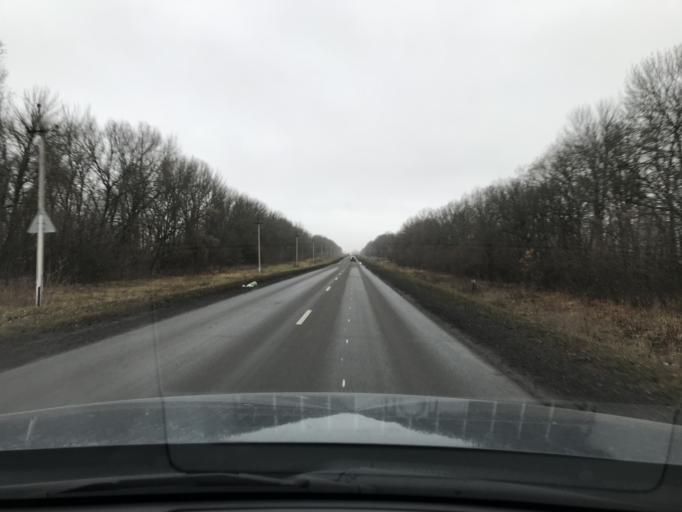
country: RU
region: Penza
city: Zemetchino
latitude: 53.5218
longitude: 42.6511
